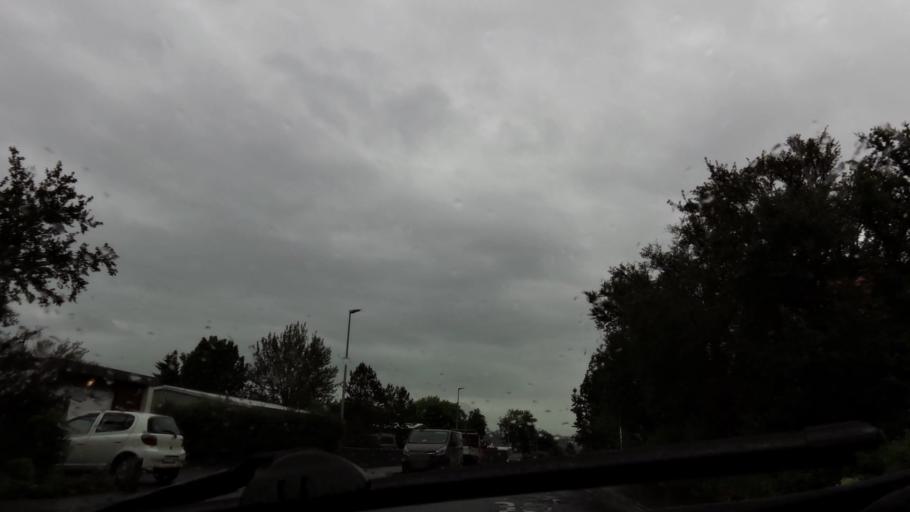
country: IS
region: Capital Region
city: Reykjavik
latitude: 64.1240
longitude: -21.8612
